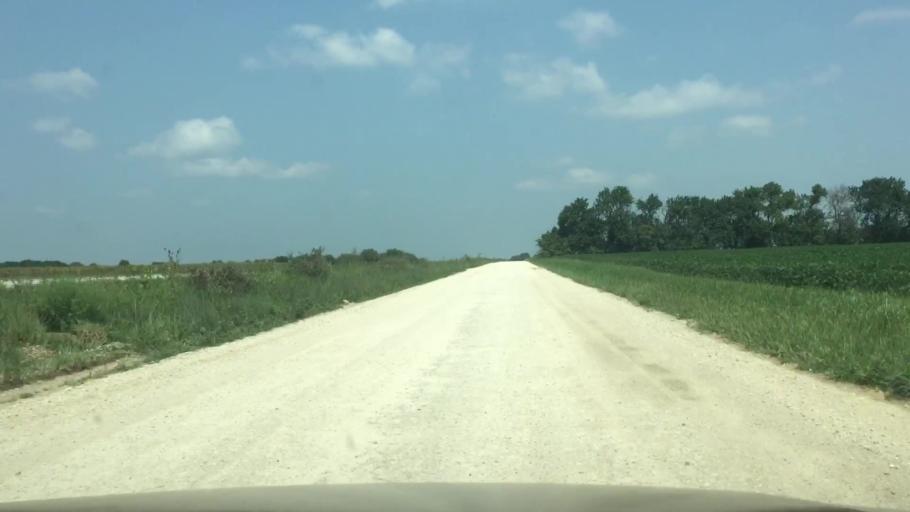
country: US
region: Kansas
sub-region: Allen County
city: Humboldt
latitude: 37.8370
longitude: -95.4093
